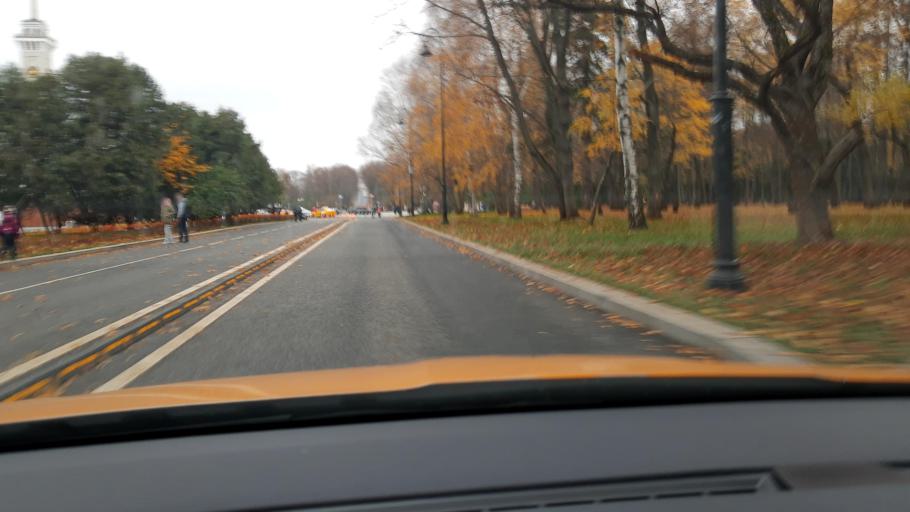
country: RU
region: Moskovskaya
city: Levoberezhnyy
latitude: 55.8498
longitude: 37.4691
